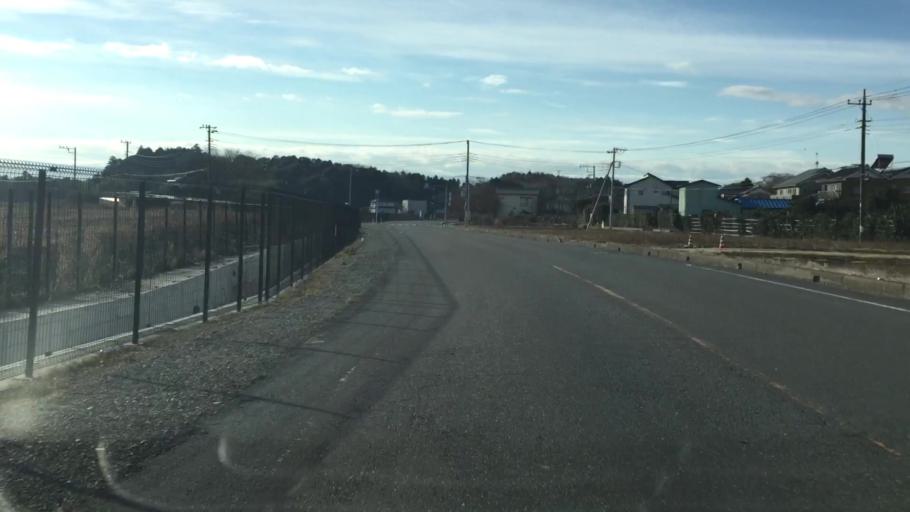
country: JP
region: Chiba
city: Shiroi
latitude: 35.8363
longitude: 140.1279
